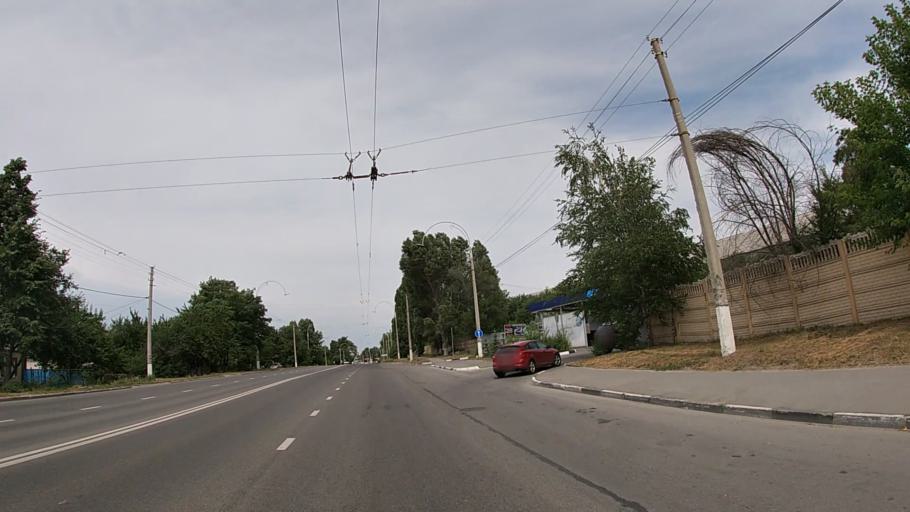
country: RU
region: Belgorod
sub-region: Belgorodskiy Rayon
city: Belgorod
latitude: 50.6079
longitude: 36.5489
